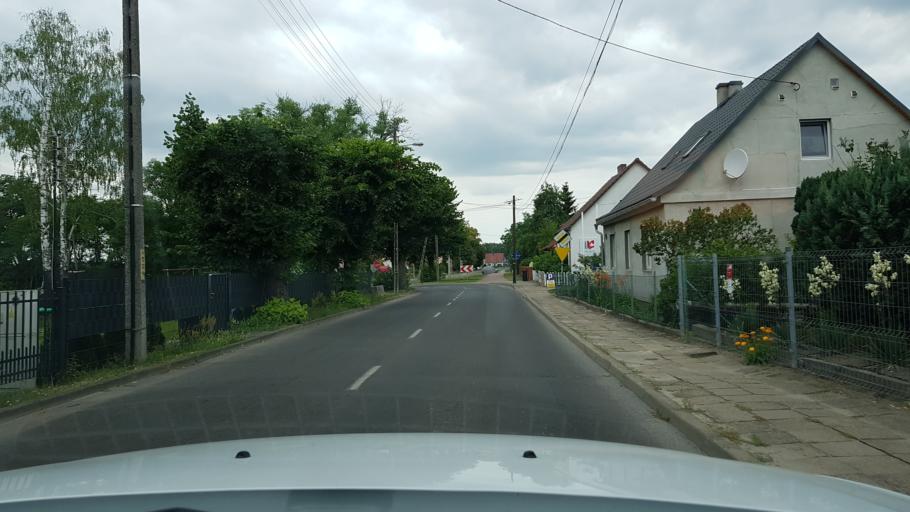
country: PL
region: Lubusz
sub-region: Powiat gorzowski
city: Kostrzyn nad Odra
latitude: 52.6139
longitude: 14.6193
